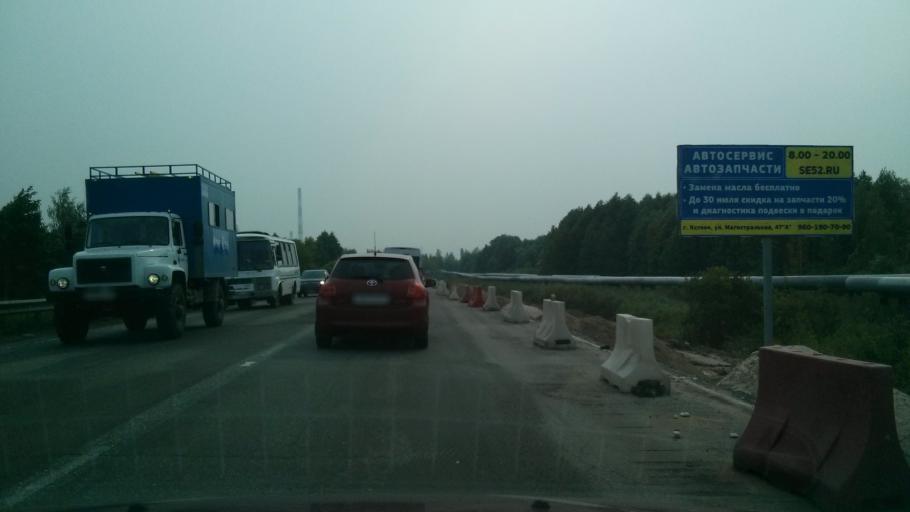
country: RU
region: Nizjnij Novgorod
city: Kstovo
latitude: 56.1237
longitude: 44.1614
